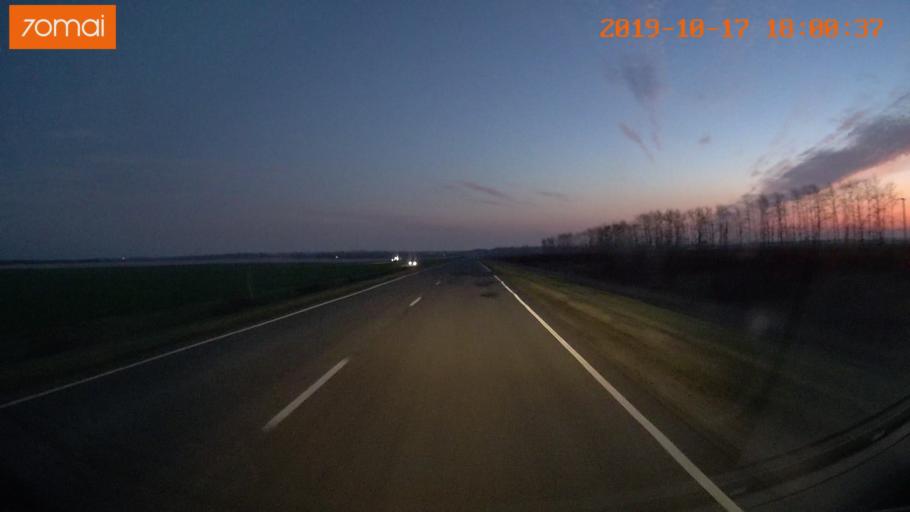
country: RU
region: Tula
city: Kurkino
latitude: 53.5191
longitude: 38.6144
